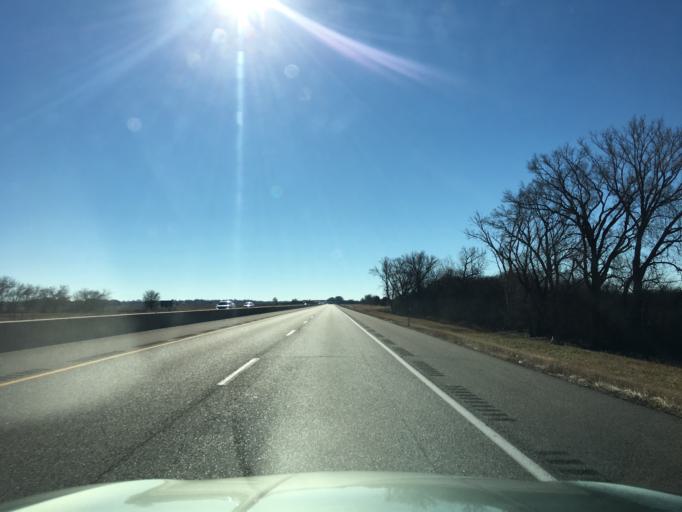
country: US
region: Kansas
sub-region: Sumner County
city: Belle Plaine
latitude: 37.4594
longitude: -97.3226
